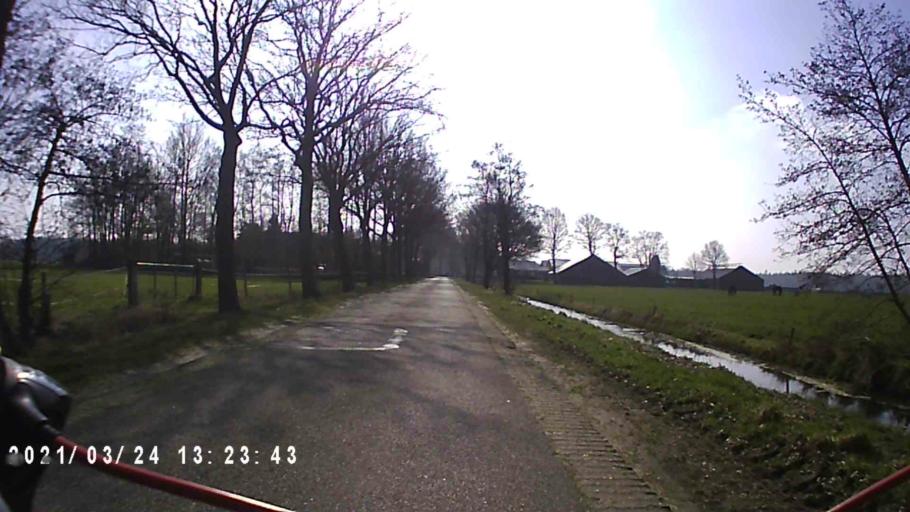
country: NL
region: Groningen
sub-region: Gemeente Grootegast
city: Grootegast
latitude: 53.0983
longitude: 6.2763
